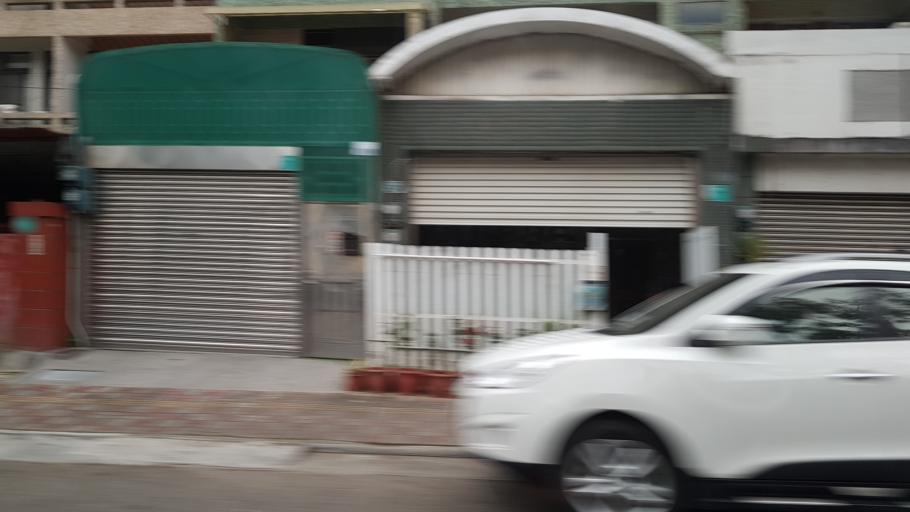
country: TW
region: Taiwan
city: Xinying
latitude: 23.3111
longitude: 120.3123
